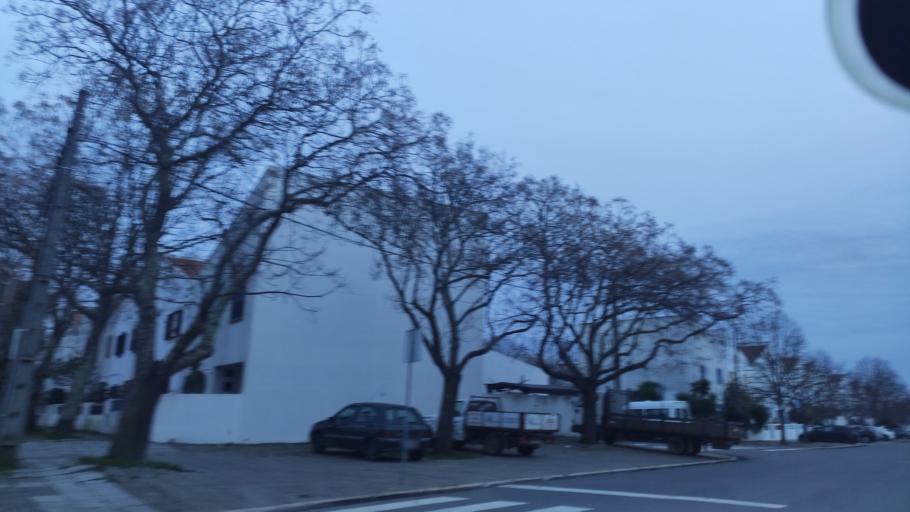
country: PT
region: Beja
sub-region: Beja
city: Beja
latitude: 38.0194
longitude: -7.8517
